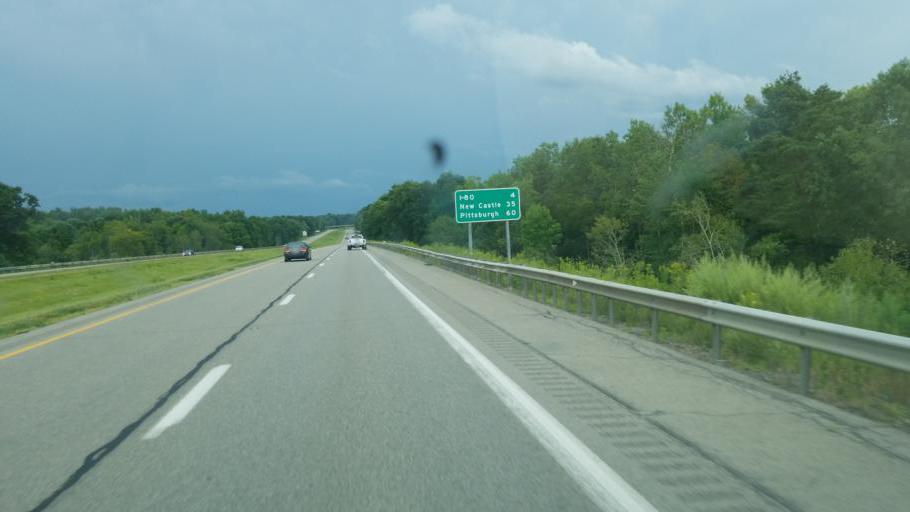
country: US
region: Pennsylvania
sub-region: Mercer County
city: Mercer
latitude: 41.2551
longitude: -80.1644
